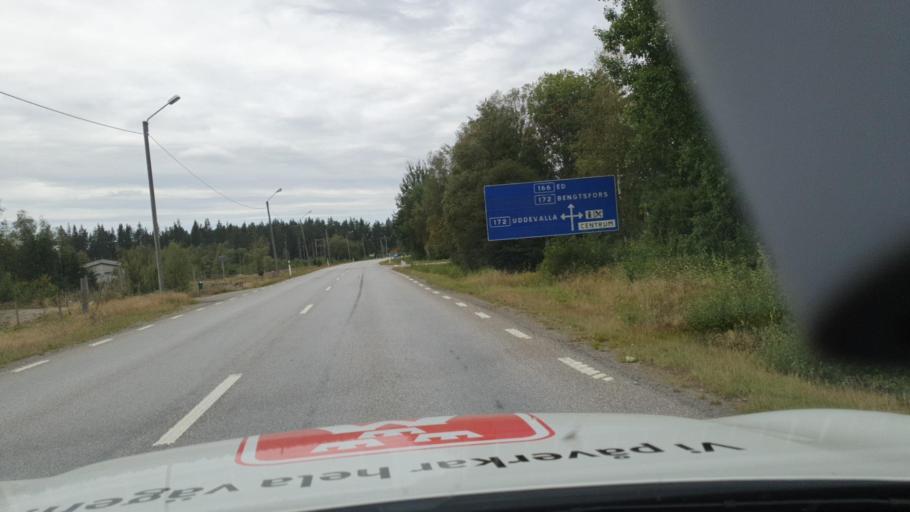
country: SE
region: Vaestra Goetaland
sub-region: Bengtsfors Kommun
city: Dals Langed
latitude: 58.8013
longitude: 12.1585
